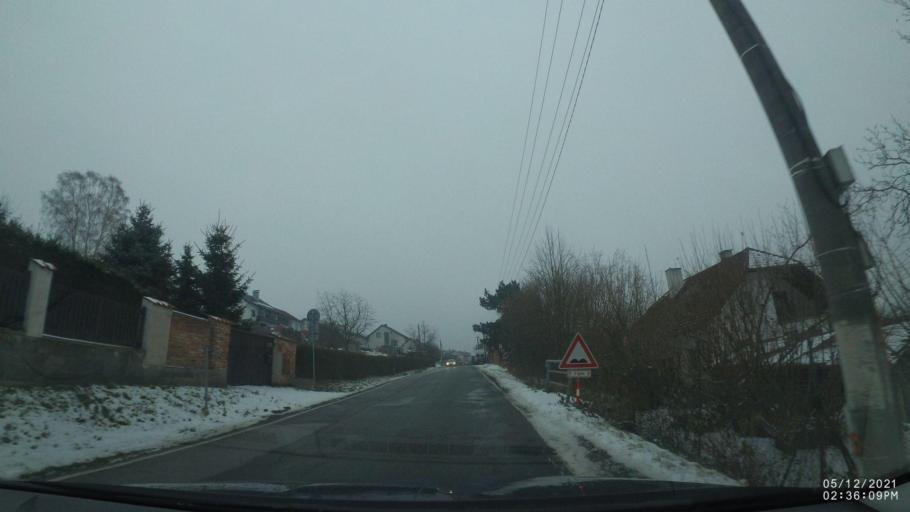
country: CZ
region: Kralovehradecky
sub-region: Okres Nachod
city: Nachod
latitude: 50.3968
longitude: 16.1725
